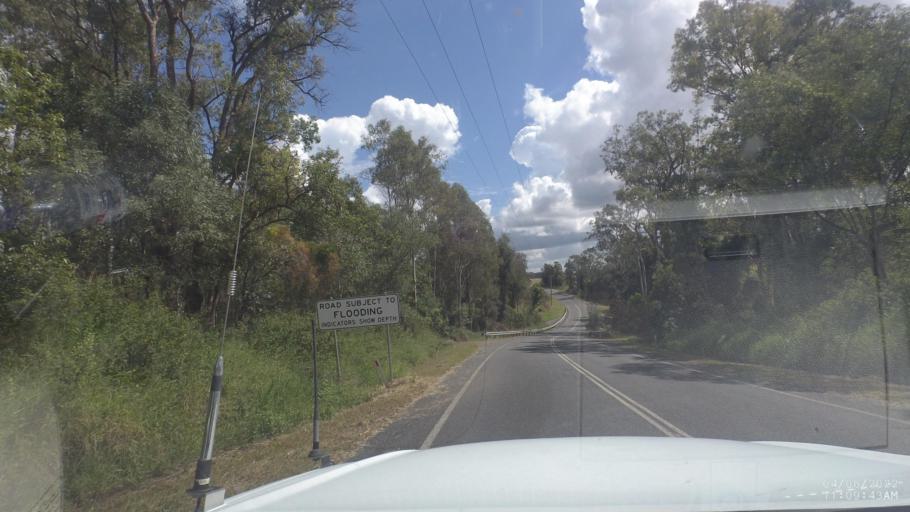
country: AU
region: Queensland
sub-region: Logan
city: Chambers Flat
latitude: -27.7743
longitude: 153.0725
